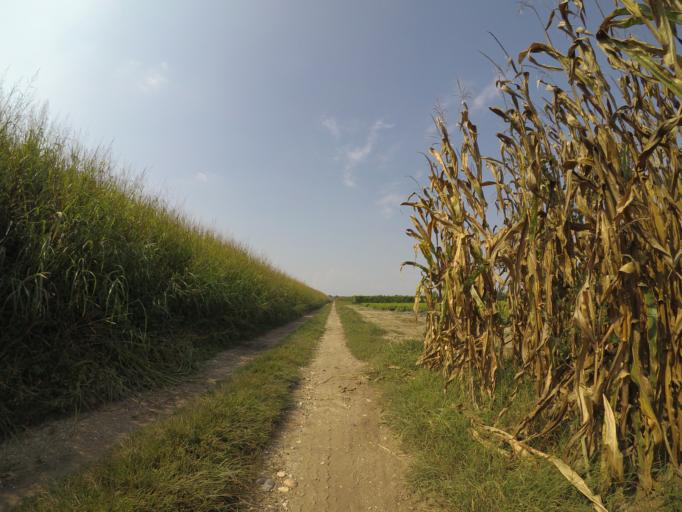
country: IT
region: Friuli Venezia Giulia
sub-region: Provincia di Udine
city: Varmo
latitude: 45.8845
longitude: 12.9701
